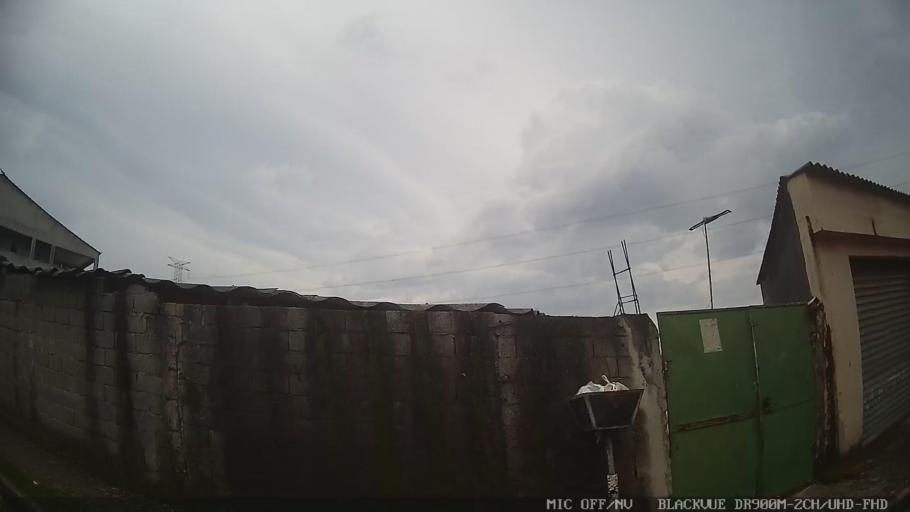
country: BR
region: Sao Paulo
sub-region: Itaquaquecetuba
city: Itaquaquecetuba
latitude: -23.4523
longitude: -46.3033
